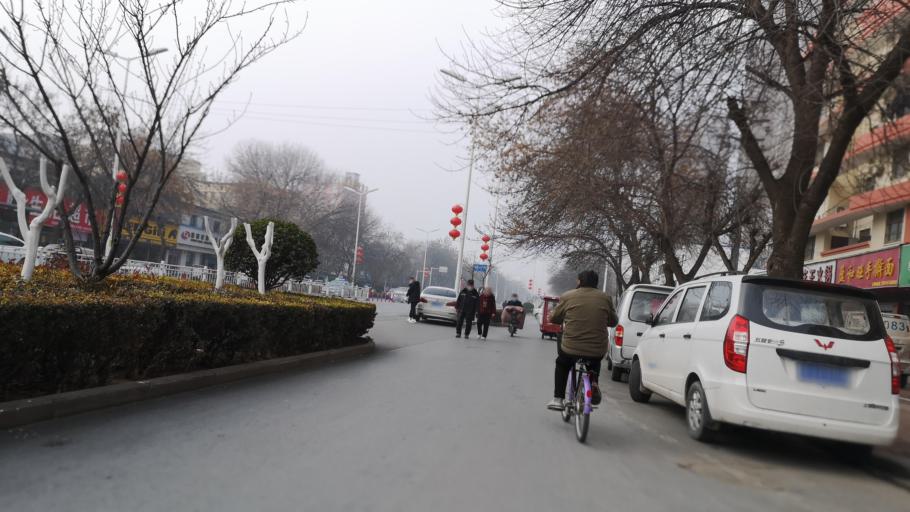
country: CN
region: Henan Sheng
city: Puyang
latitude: 35.7722
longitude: 115.0370
